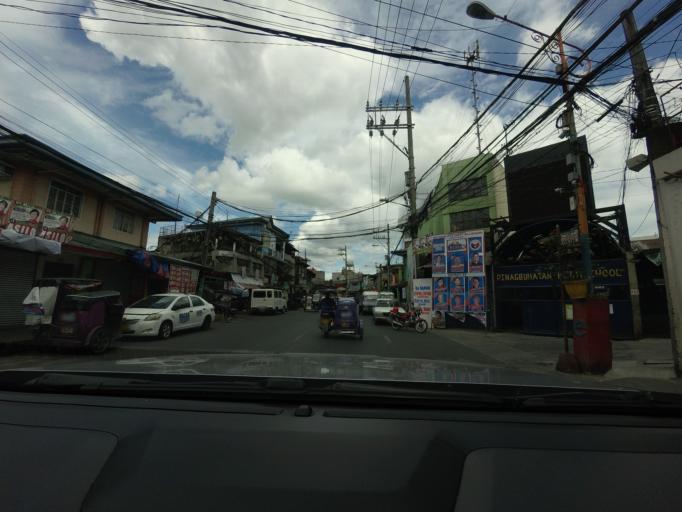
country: PH
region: Calabarzon
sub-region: Province of Rizal
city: Pateros
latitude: 14.5551
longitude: 121.0911
